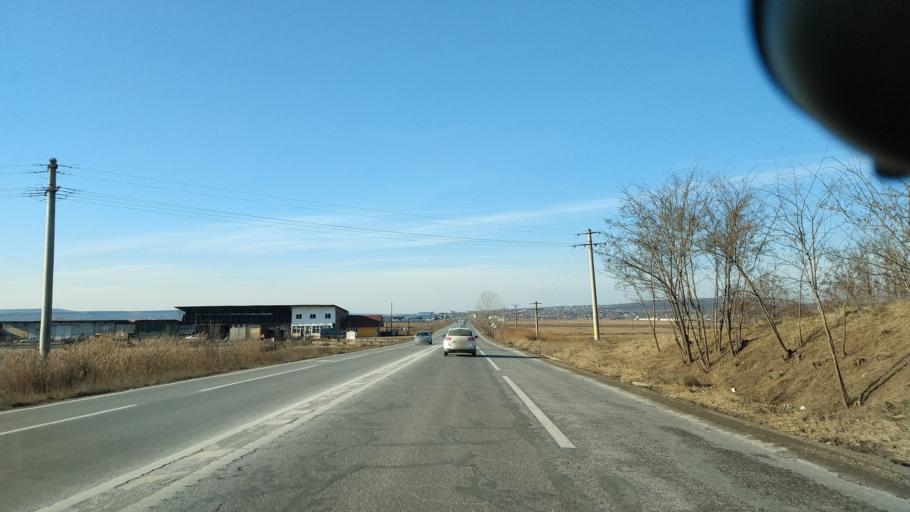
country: RO
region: Iasi
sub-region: Comuna Letcani
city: Letcani
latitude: 47.1863
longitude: 27.4479
